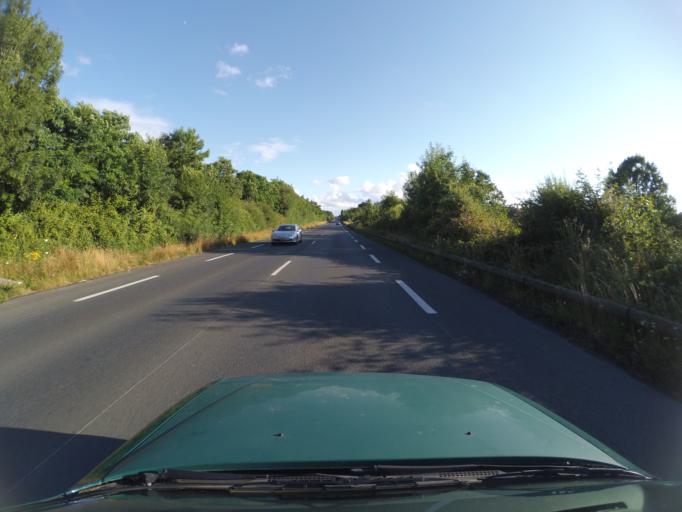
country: FR
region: Pays de la Loire
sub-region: Departement de la Vendee
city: Saint-Hilaire-de-Loulay
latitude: 46.9966
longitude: -1.3484
